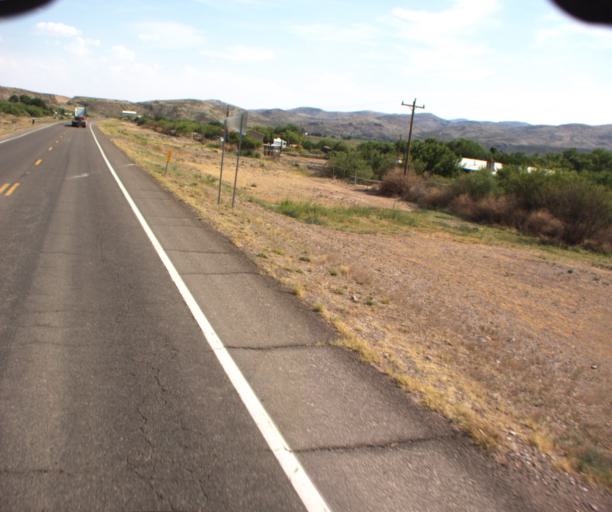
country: US
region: Arizona
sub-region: Greenlee County
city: Clifton
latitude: 32.9120
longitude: -109.1972
